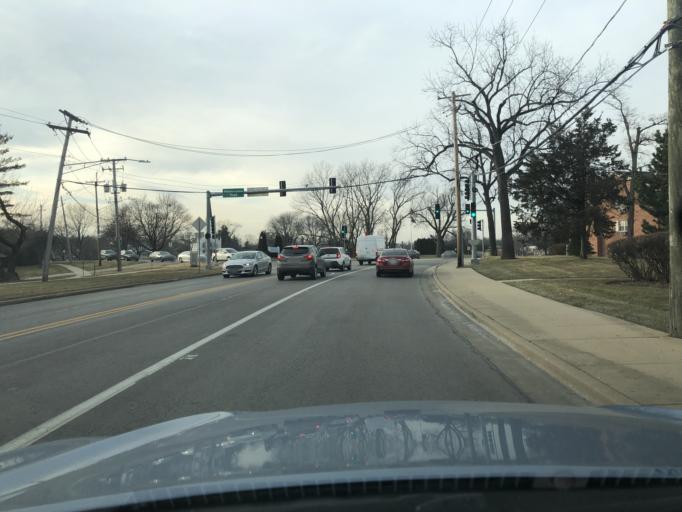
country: US
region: Illinois
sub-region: DuPage County
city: Itasca
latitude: 41.9685
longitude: -88.0100
